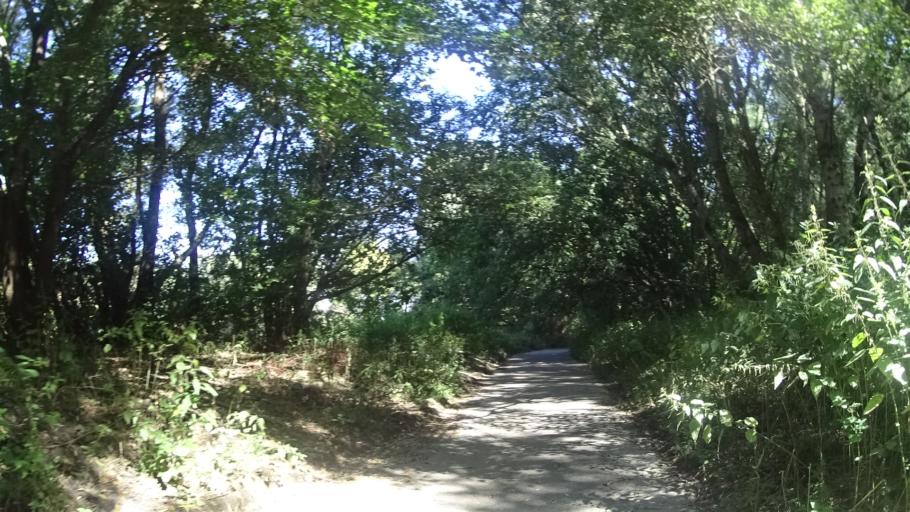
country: AT
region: Lower Austria
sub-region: Politischer Bezirk Bruck an der Leitha
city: Hainburg an der Donau
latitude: 48.1785
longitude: 16.9767
